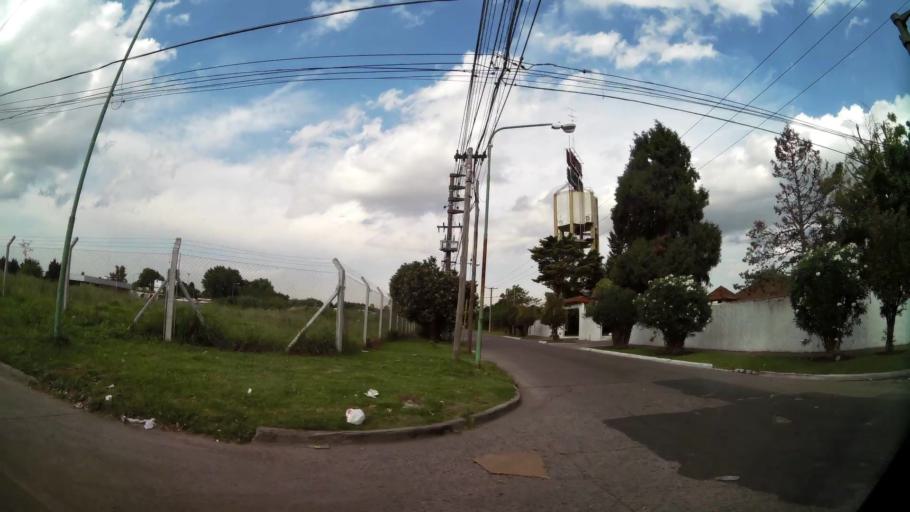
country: AR
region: Buenos Aires
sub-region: Partido de Tigre
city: Tigre
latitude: -34.4750
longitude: -58.6561
